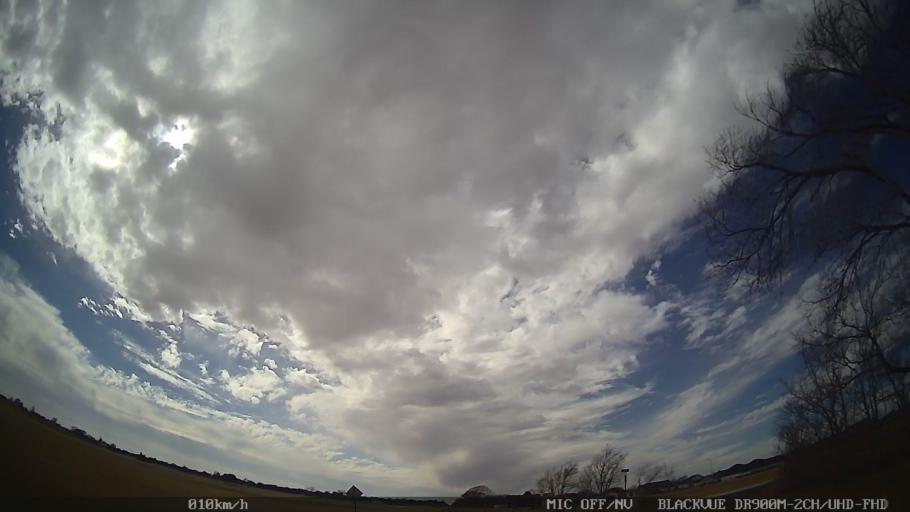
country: US
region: New Mexico
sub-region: Curry County
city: Clovis
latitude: 34.4198
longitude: -103.1621
